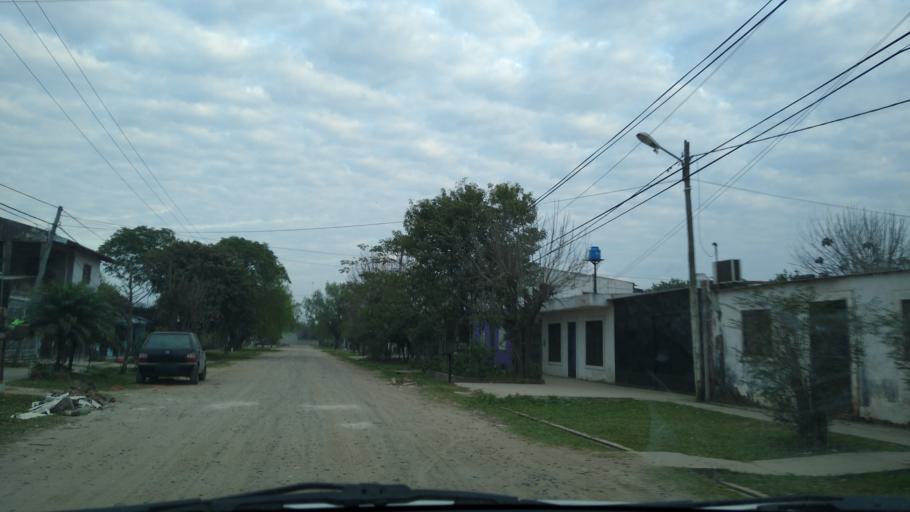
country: AR
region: Chaco
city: Resistencia
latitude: -27.4774
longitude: -58.9696
